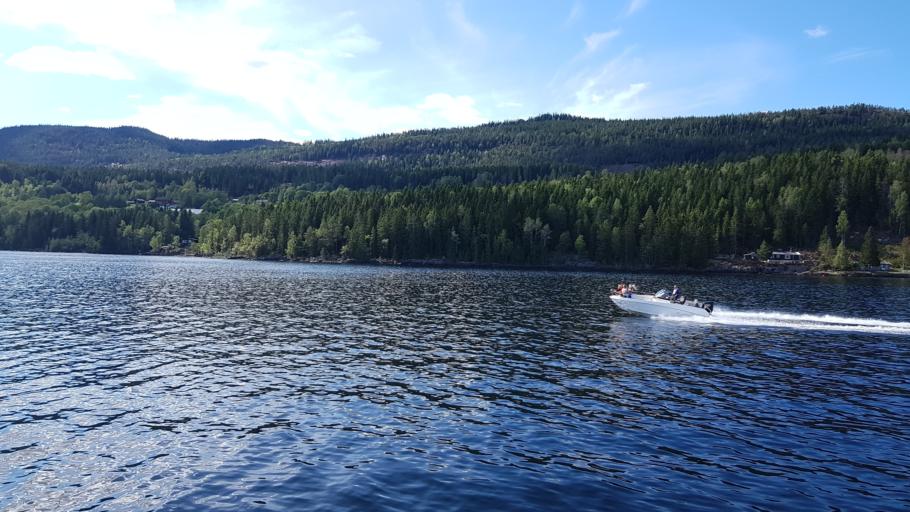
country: NO
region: Akershus
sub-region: Hurdal
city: Hurdal
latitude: 60.5421
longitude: 11.1989
